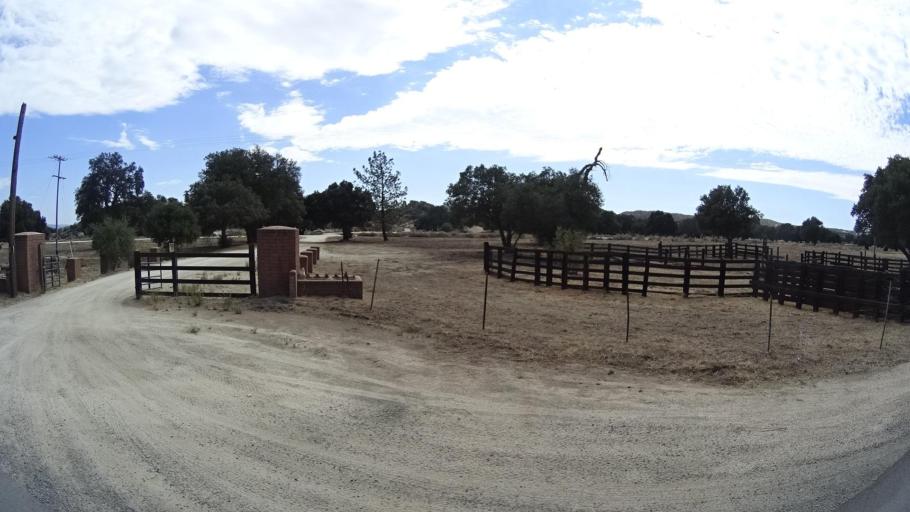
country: MX
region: Baja California
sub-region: Tecate
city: Cereso del Hongo
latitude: 32.6430
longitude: -116.2780
